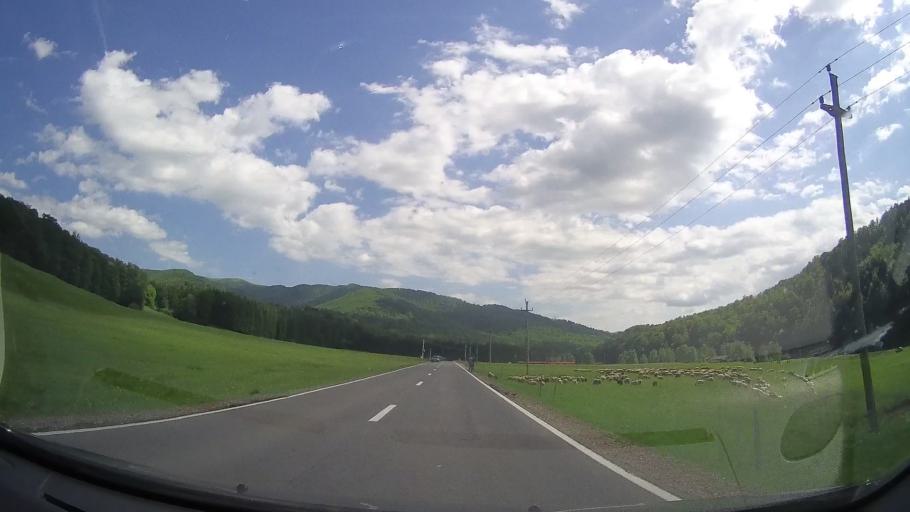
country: RO
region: Prahova
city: Maneciu
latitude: 45.4230
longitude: 25.9419
